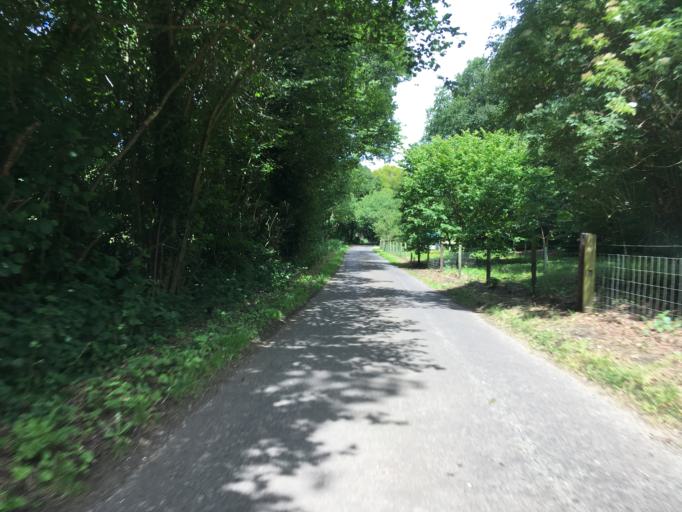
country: GB
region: England
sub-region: Hampshire
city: Highclere
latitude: 51.2895
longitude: -1.4183
